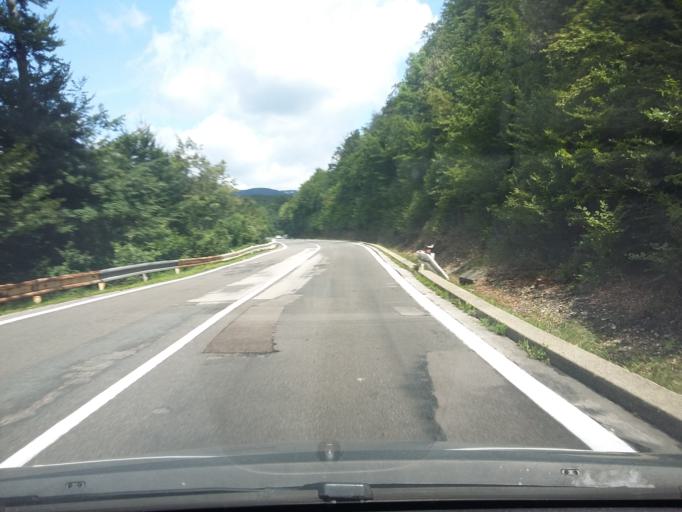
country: SK
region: Bratislavsky
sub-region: Okres Pezinok
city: Pezinok
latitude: 48.3449
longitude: 17.2202
